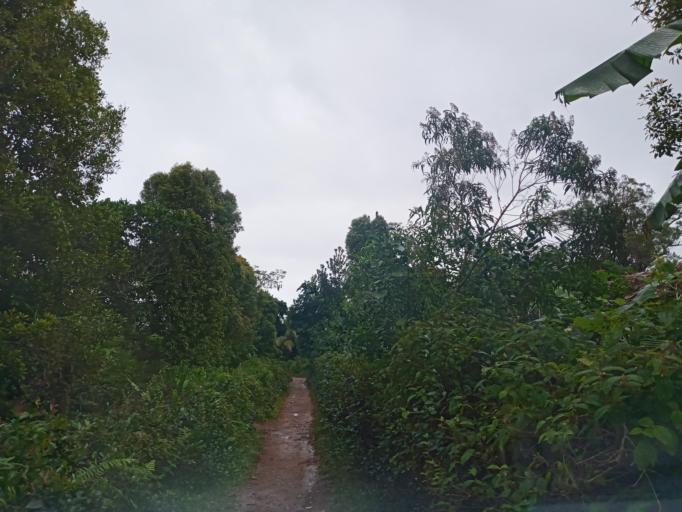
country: MG
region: Atsimo-Atsinanana
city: Vohipaho
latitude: -23.8277
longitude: 47.5437
